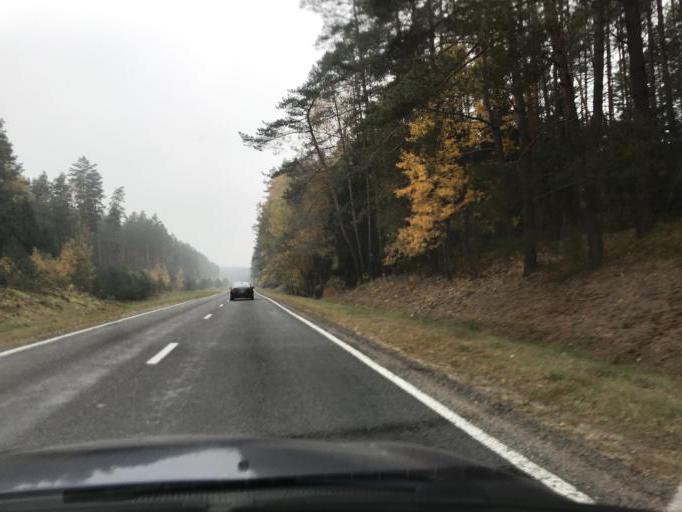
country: LT
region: Alytaus apskritis
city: Druskininkai
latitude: 53.8775
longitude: 23.9006
